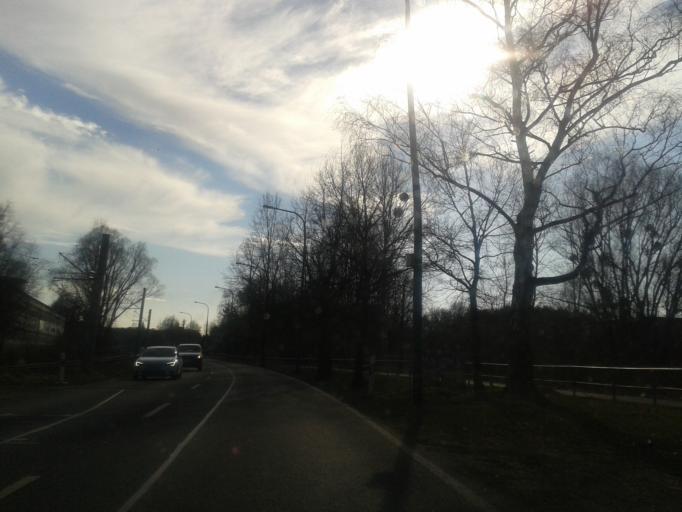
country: DE
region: Saxony
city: Albertstadt
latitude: 51.1273
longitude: 13.7924
